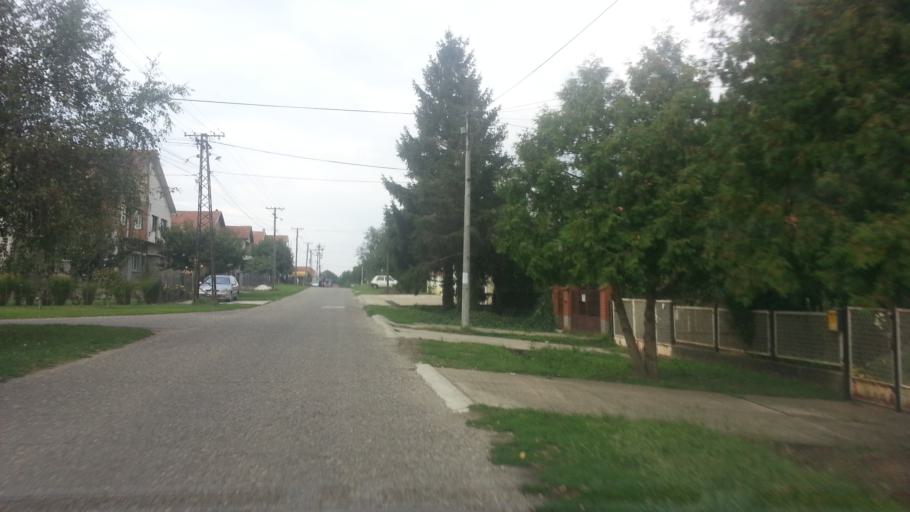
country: RS
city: Stari Banovci
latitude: 44.9767
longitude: 20.2776
